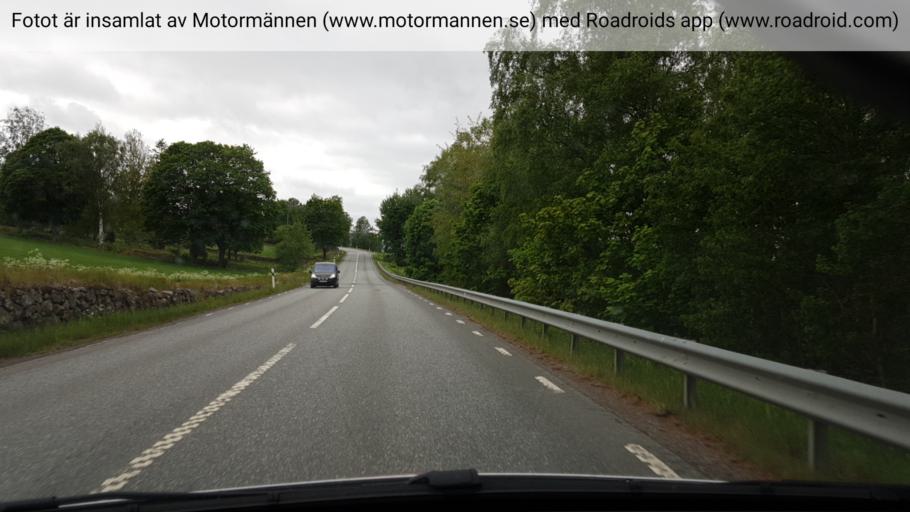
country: SE
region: Joenkoeping
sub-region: Tranas Kommun
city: Tranas
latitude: 57.9981
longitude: 14.8665
